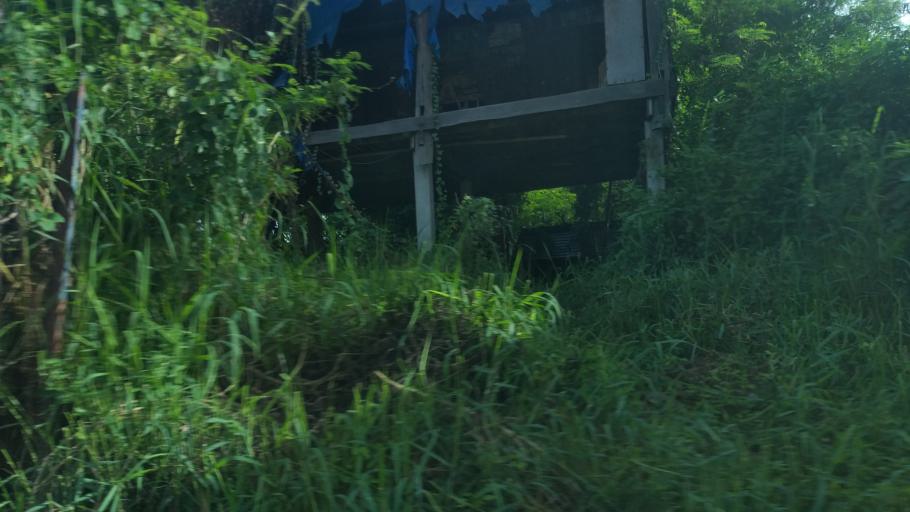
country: TH
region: Chaiyaphum
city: Ban Thaen
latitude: 16.4093
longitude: 102.3521
